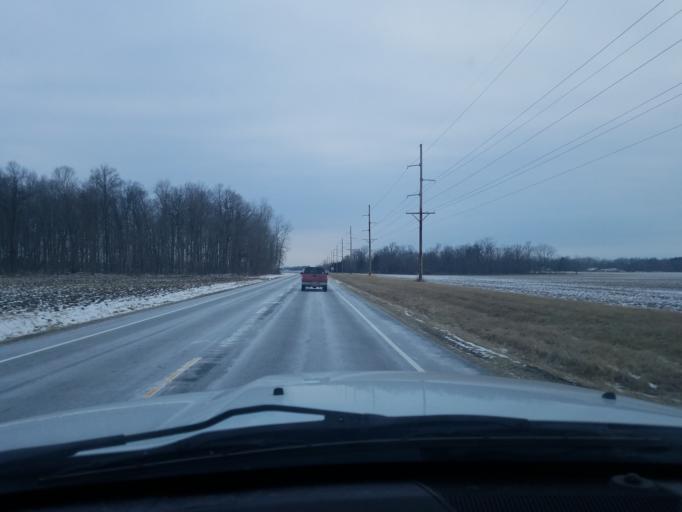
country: US
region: Indiana
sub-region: Randolph County
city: Farmland
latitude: 40.1713
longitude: -85.0857
